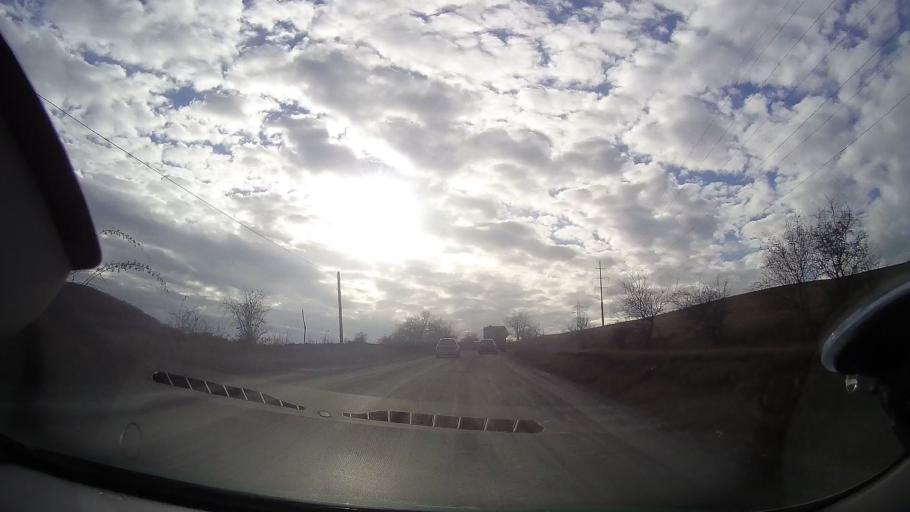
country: RO
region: Cluj
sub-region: Comuna Savadisla
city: Savadisla
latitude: 46.6554
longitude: 23.4520
